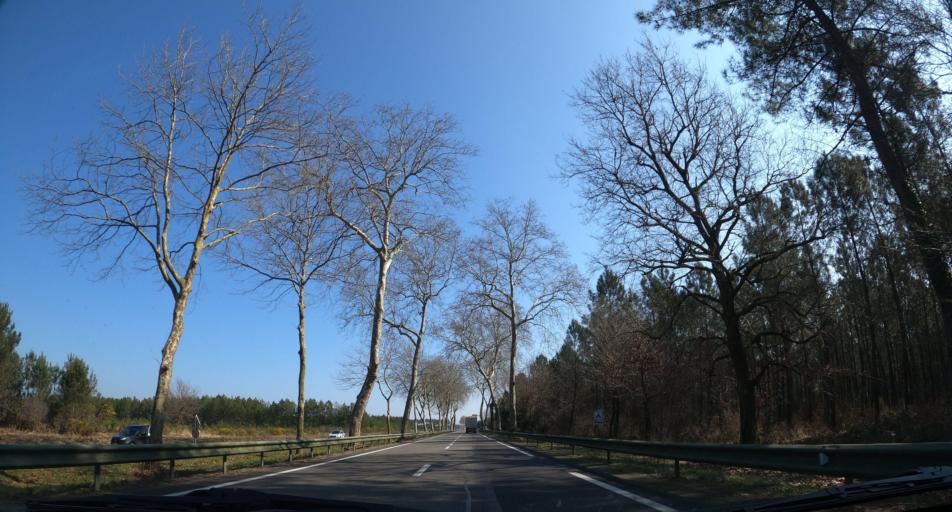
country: FR
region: Aquitaine
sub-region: Departement des Landes
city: Riviere-Saas-et-Gourby
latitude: 43.7064
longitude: -1.1685
